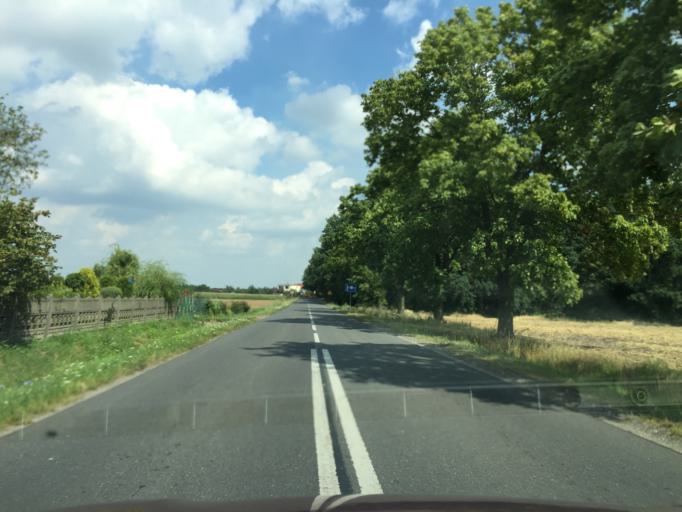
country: PL
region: Greater Poland Voivodeship
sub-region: Powiat kaliski
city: Stawiszyn
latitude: 51.9402
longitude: 18.1498
